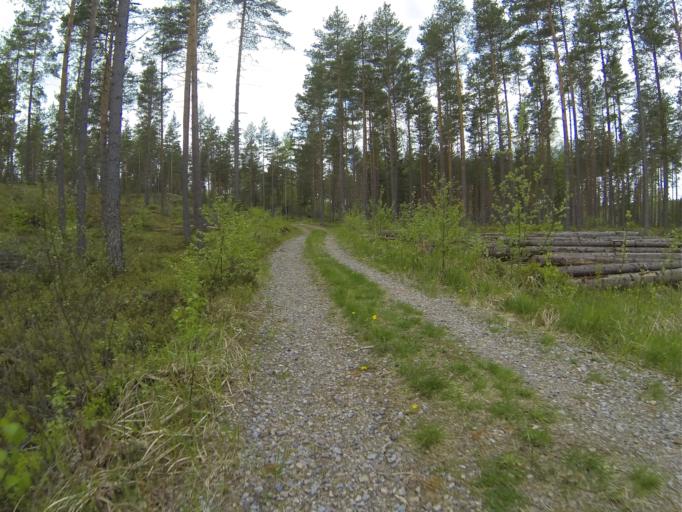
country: FI
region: Varsinais-Suomi
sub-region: Salo
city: Salo
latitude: 60.3495
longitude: 23.1001
